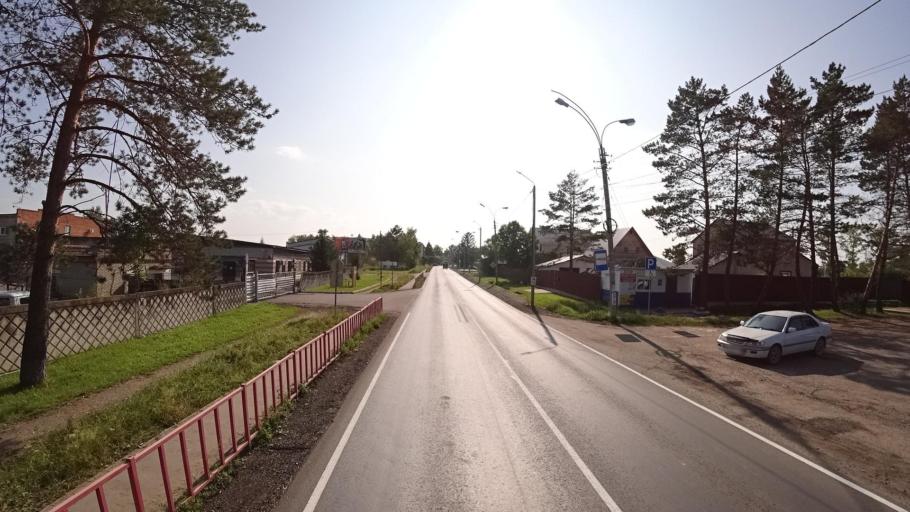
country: RU
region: Khabarovsk Krai
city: Khor
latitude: 47.9730
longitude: 135.0630
